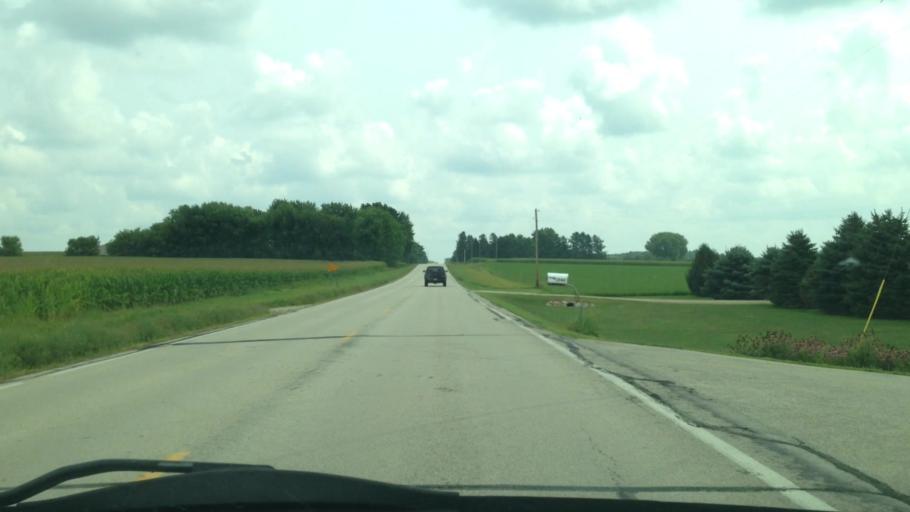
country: US
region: Minnesota
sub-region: Olmsted County
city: Rochester
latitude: 44.1369
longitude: -92.4038
